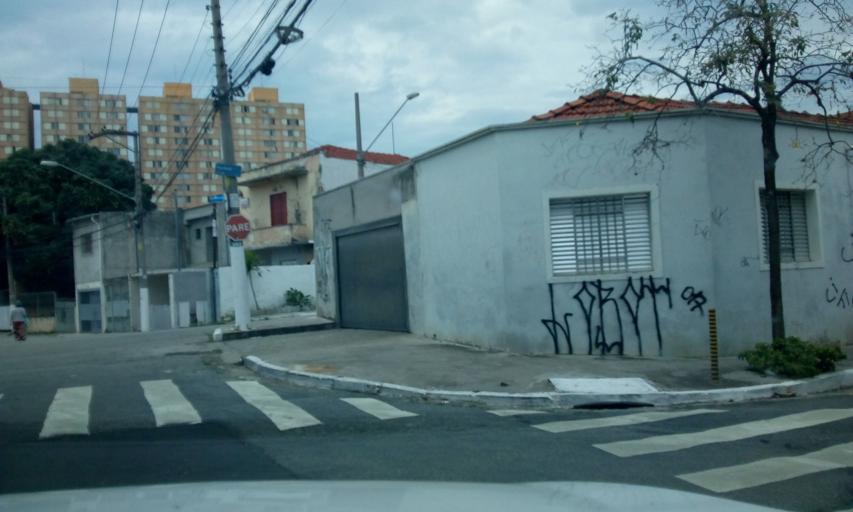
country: BR
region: Sao Paulo
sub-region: Sao Paulo
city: Sao Paulo
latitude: -23.5168
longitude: -46.7004
